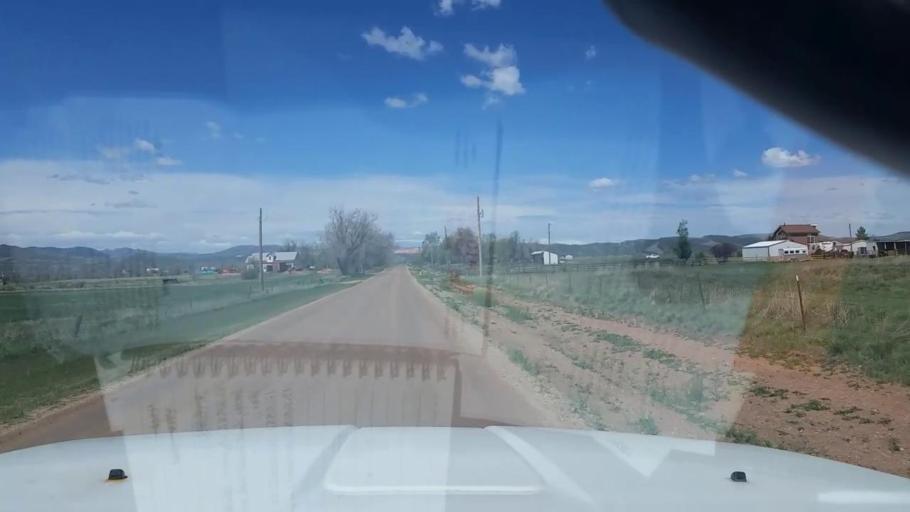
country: US
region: Colorado
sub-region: Larimer County
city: Wellington
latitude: 40.7839
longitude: -105.0876
